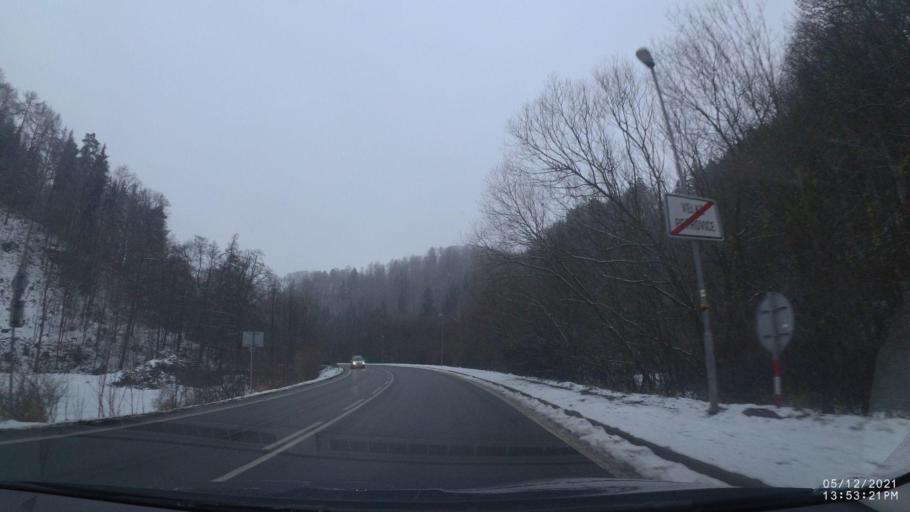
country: CZ
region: Kralovehradecky
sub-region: Okres Nachod
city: Police nad Metuji
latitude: 50.5179
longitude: 16.2133
